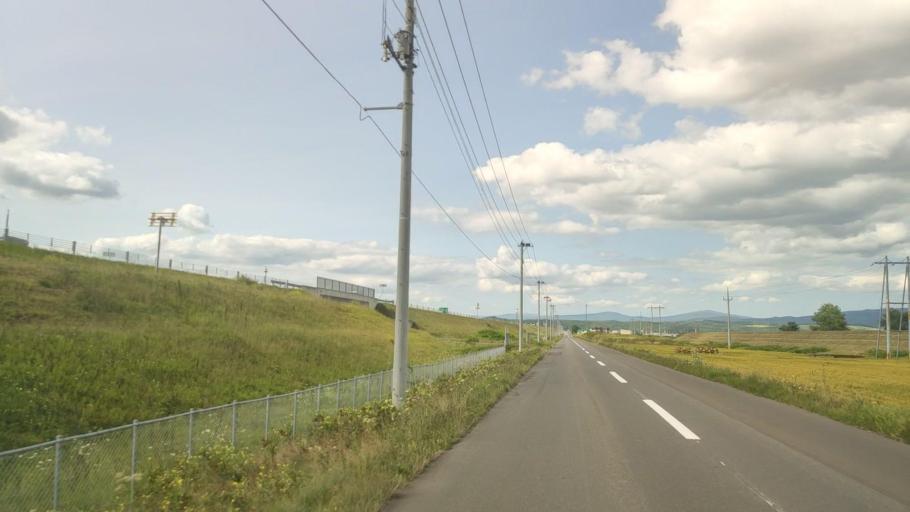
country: JP
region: Hokkaido
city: Nayoro
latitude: 44.3505
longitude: 142.4362
